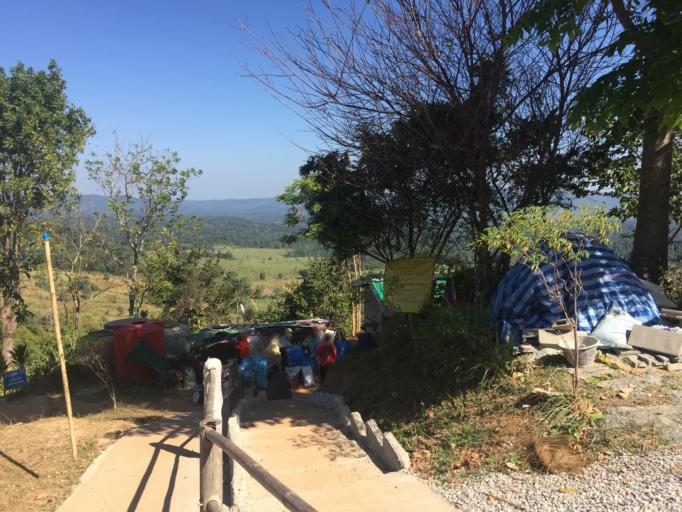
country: TH
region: Phetchabun
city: Khao Kho
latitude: 16.5851
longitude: 100.9316
